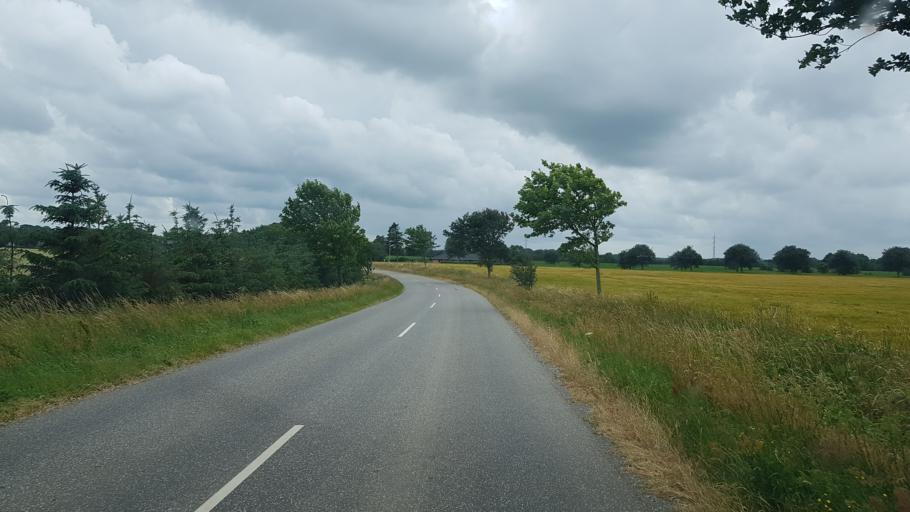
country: DK
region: South Denmark
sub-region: Kolding Kommune
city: Vamdrup
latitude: 55.4391
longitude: 9.2641
